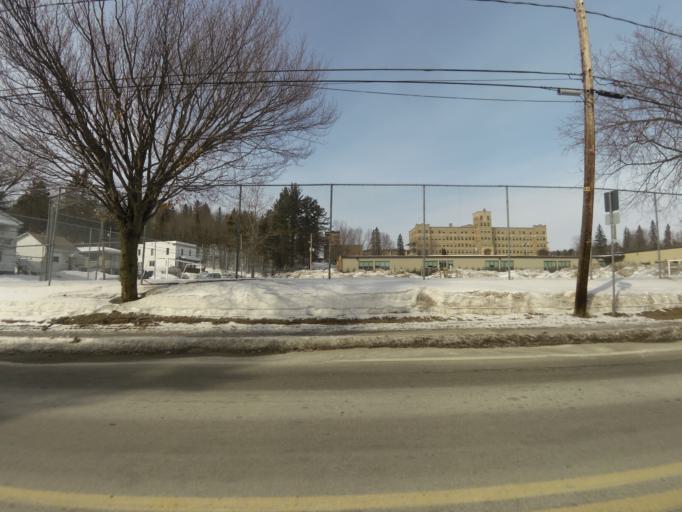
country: CA
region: Quebec
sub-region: Laurentides
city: Mont-Laurier
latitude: 46.5566
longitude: -75.5001
